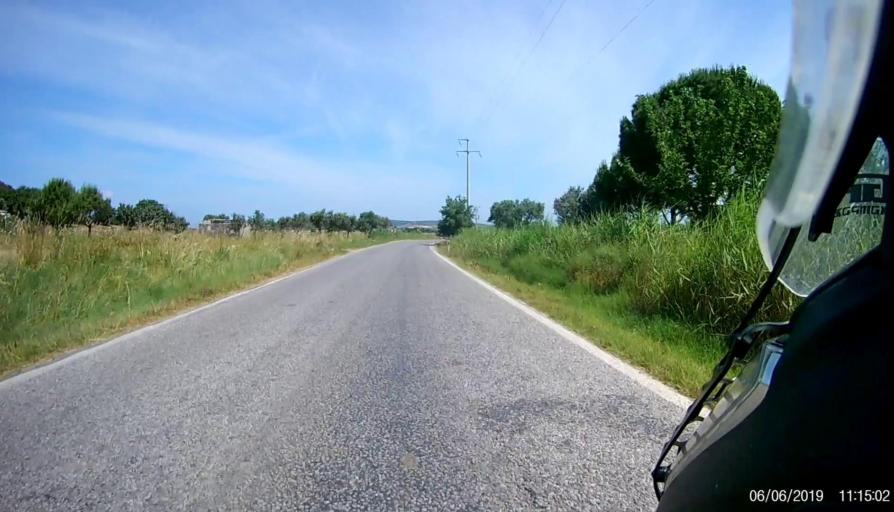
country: TR
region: Canakkale
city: Gulpinar
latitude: 39.6268
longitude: 26.1825
